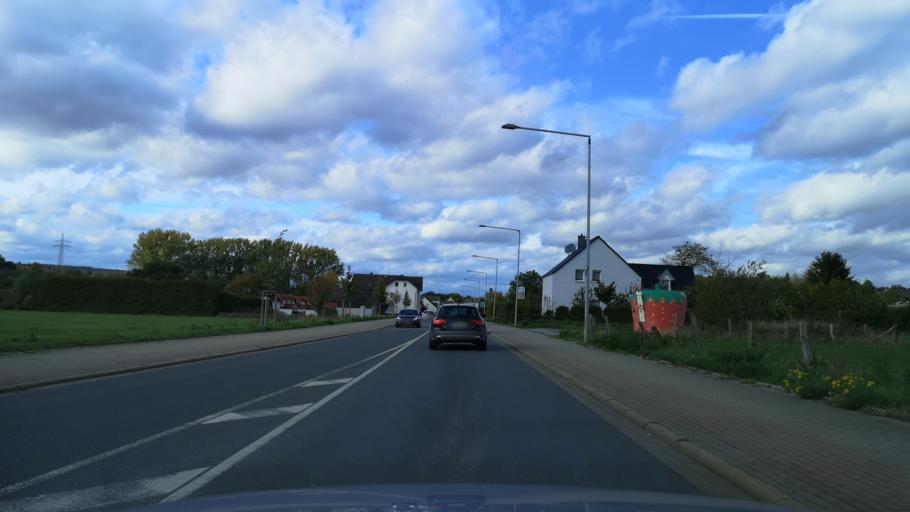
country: DE
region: North Rhine-Westphalia
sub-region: Regierungsbezirk Arnsberg
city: Menden
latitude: 51.4187
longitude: 7.8275
